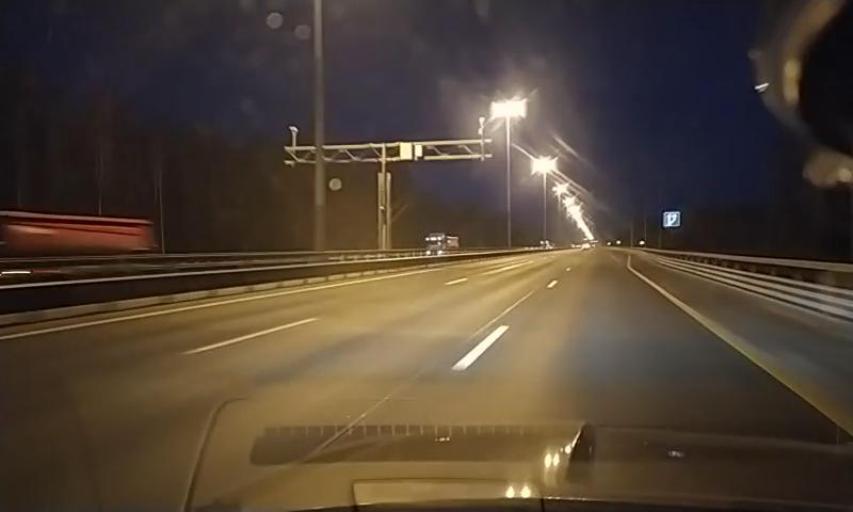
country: RU
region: St.-Petersburg
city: Pesochnyy
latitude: 60.0939
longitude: 30.0961
